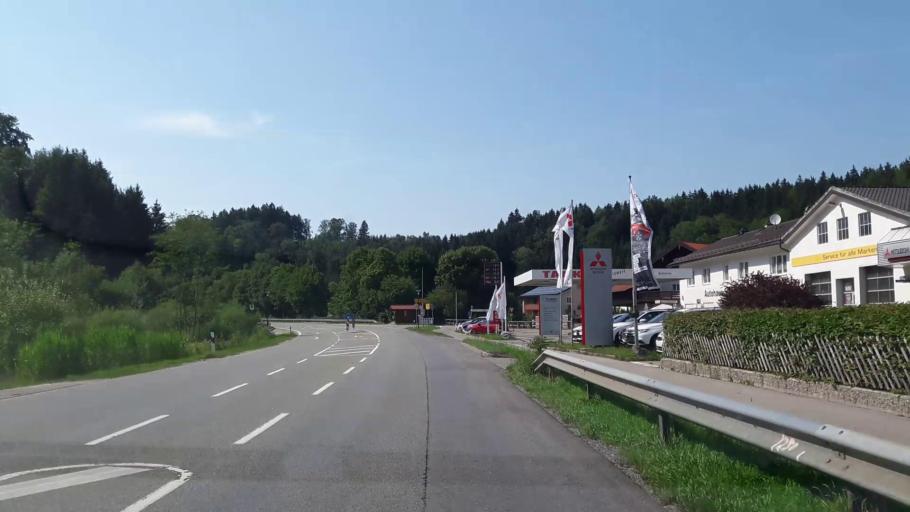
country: DE
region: Bavaria
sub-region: Upper Bavaria
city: Traunstein
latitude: 47.8683
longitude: 12.6693
